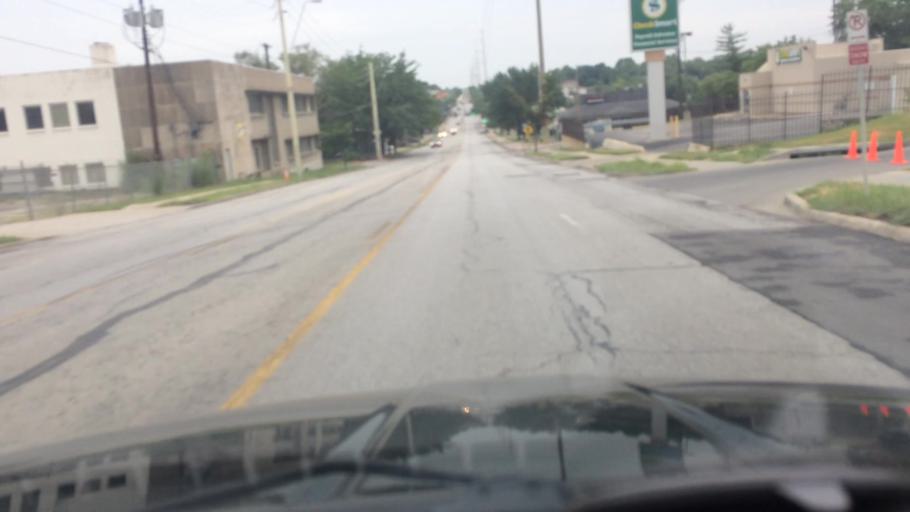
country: US
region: Kansas
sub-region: Johnson County
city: Mission Hills
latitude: 39.0088
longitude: -94.5748
